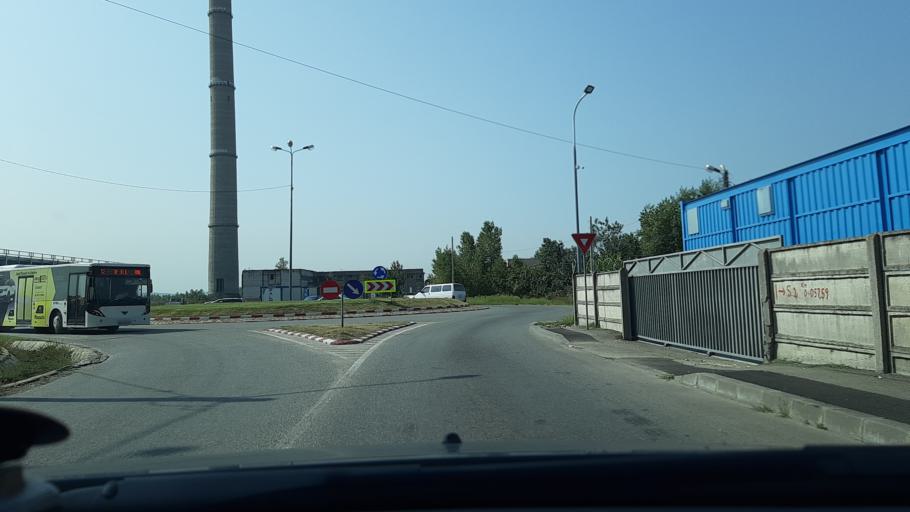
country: RO
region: Gorj
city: Targu Jiu
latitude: 45.0167
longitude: 23.2596
